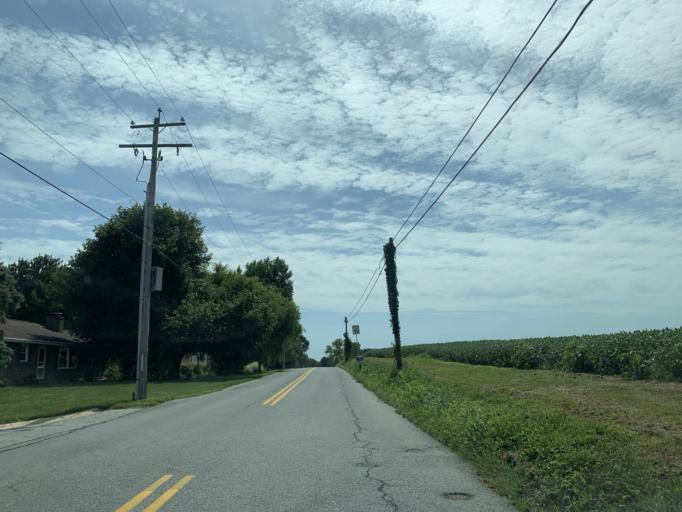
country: US
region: Pennsylvania
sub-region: York County
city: Spry
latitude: 39.9033
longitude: -76.6946
